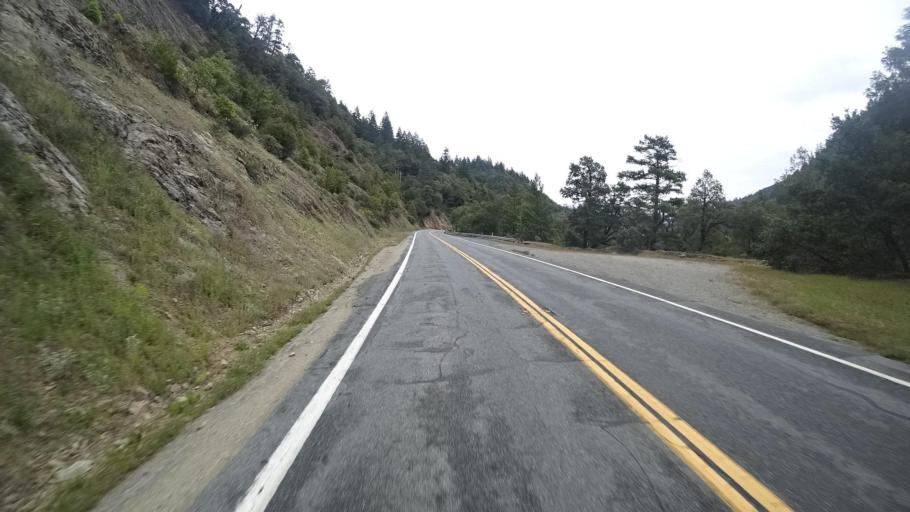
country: US
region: California
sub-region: Humboldt County
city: Willow Creek
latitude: 41.2587
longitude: -123.6198
